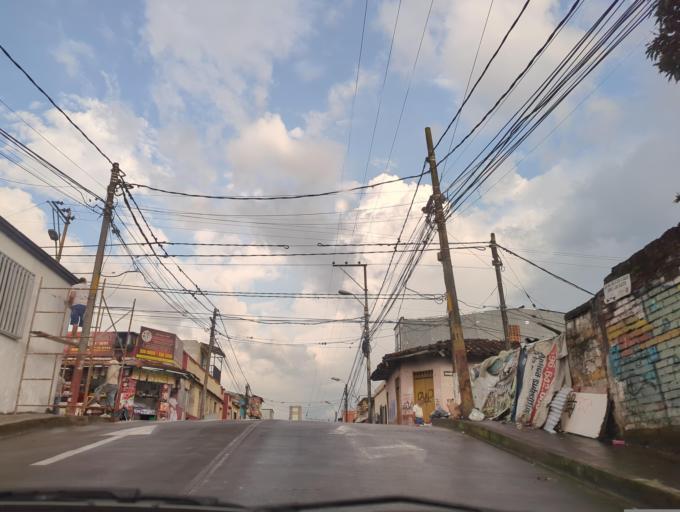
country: CO
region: Risaralda
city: Pereira
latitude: 4.8133
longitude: -75.7039
